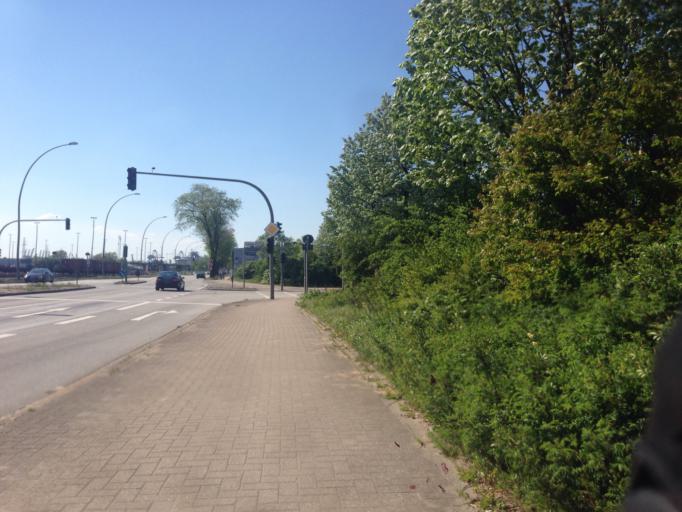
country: DE
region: Hamburg
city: Kleiner Grasbrook
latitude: 53.5268
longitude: 9.9868
